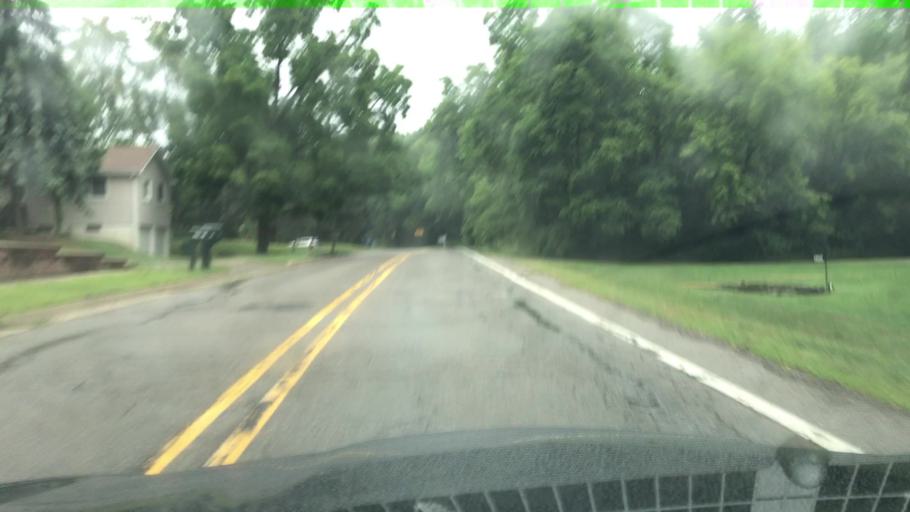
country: US
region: Michigan
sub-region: Oakland County
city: Auburn Hills
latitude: 42.7250
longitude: -83.2728
